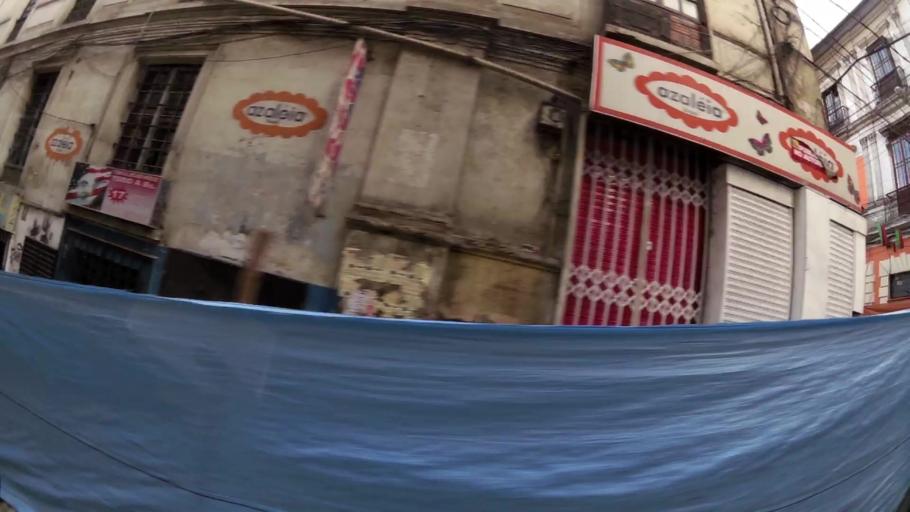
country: BO
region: La Paz
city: La Paz
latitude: -16.4950
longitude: -68.1356
